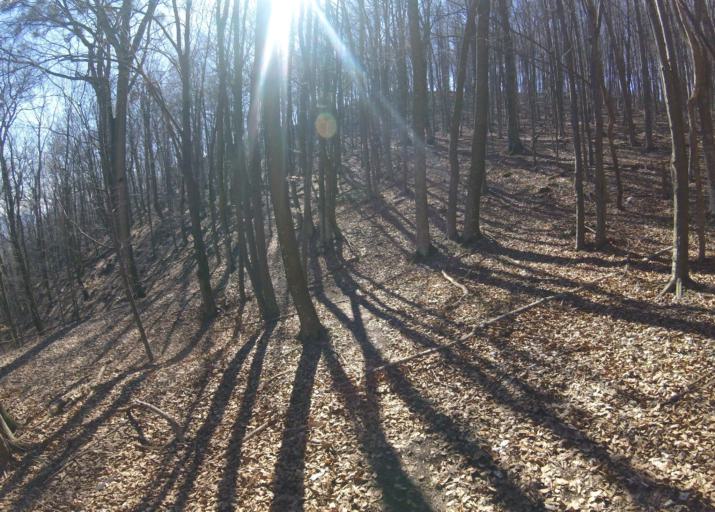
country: HU
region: Heves
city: Szilvasvarad
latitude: 48.0530
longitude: 20.4340
